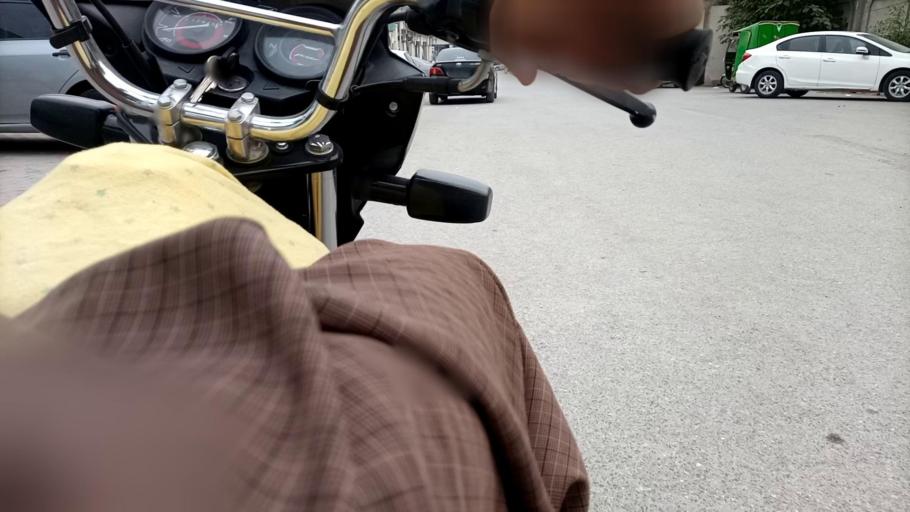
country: PK
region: Khyber Pakhtunkhwa
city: Peshawar
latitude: 34.0031
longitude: 71.5453
